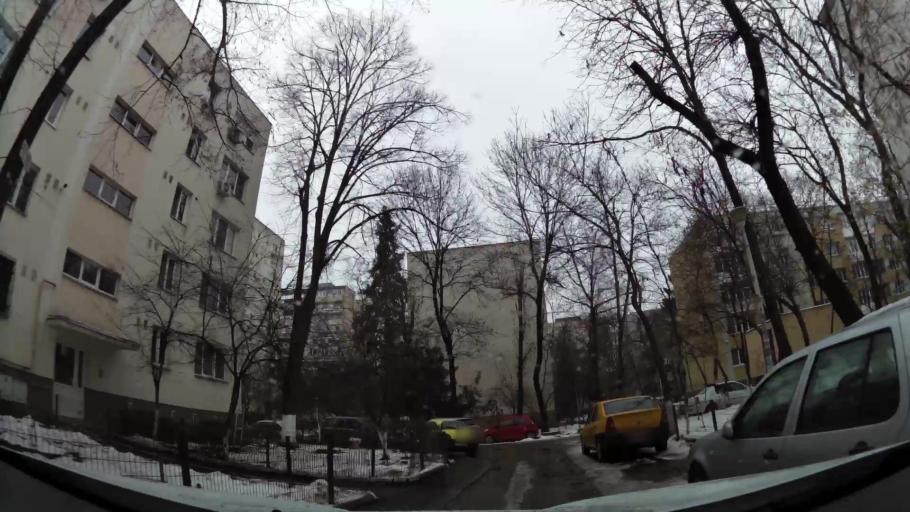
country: RO
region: Ilfov
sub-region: Comuna Chiajna
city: Rosu
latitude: 44.4157
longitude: 26.0200
